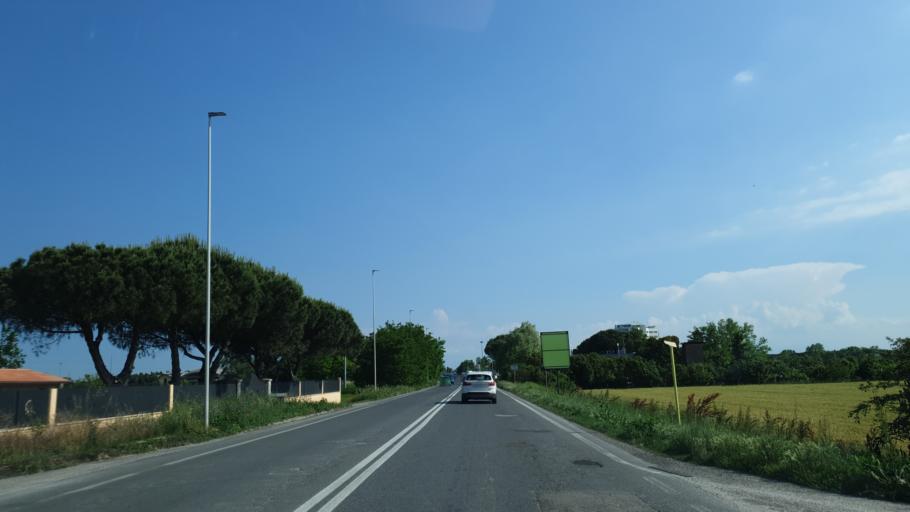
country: IT
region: Emilia-Romagna
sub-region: Provincia di Ravenna
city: Ravenna
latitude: 44.4410
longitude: 12.2111
